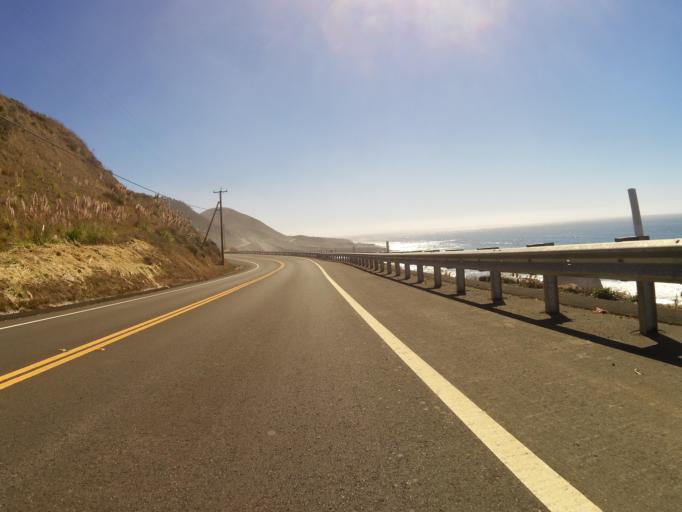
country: US
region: California
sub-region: Mendocino County
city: Fort Bragg
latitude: 39.6189
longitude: -123.7817
